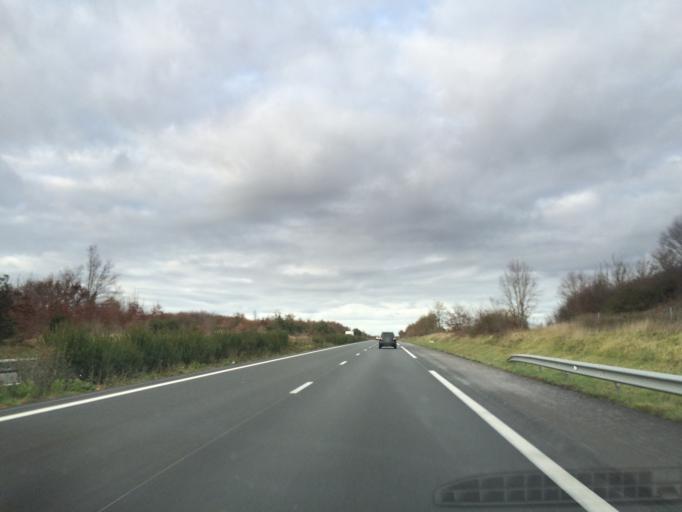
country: FR
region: Poitou-Charentes
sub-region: Departement des Deux-Sevres
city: Beauvoir-sur-Niort
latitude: 46.0900
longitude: -0.5325
